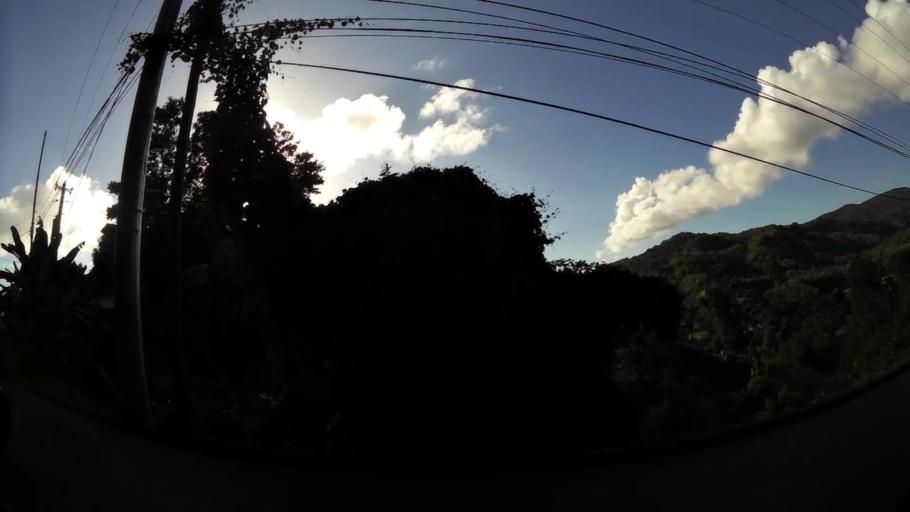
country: TT
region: Eastern Tobago
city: Roxborough
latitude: 11.2240
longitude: -60.6129
